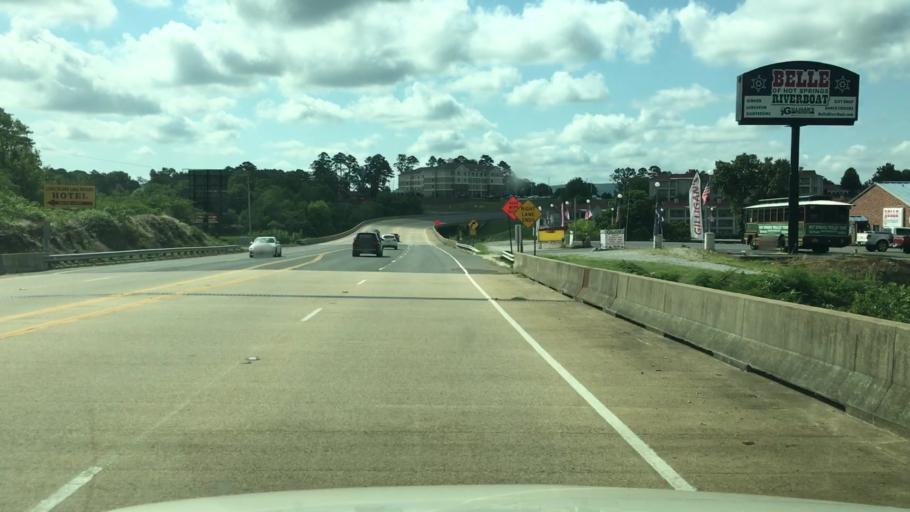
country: US
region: Arkansas
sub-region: Garland County
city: Lake Hamilton
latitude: 34.4317
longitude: -93.0865
